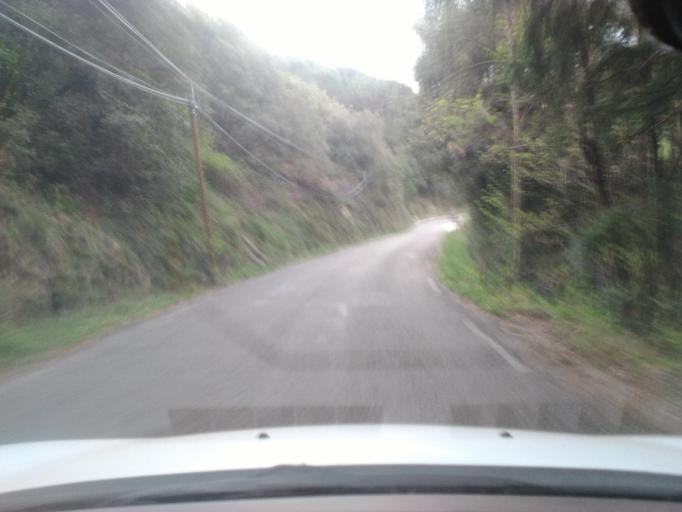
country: FR
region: Languedoc-Roussillon
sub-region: Departement du Gard
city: Lasalle
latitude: 44.0629
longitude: 3.8378
